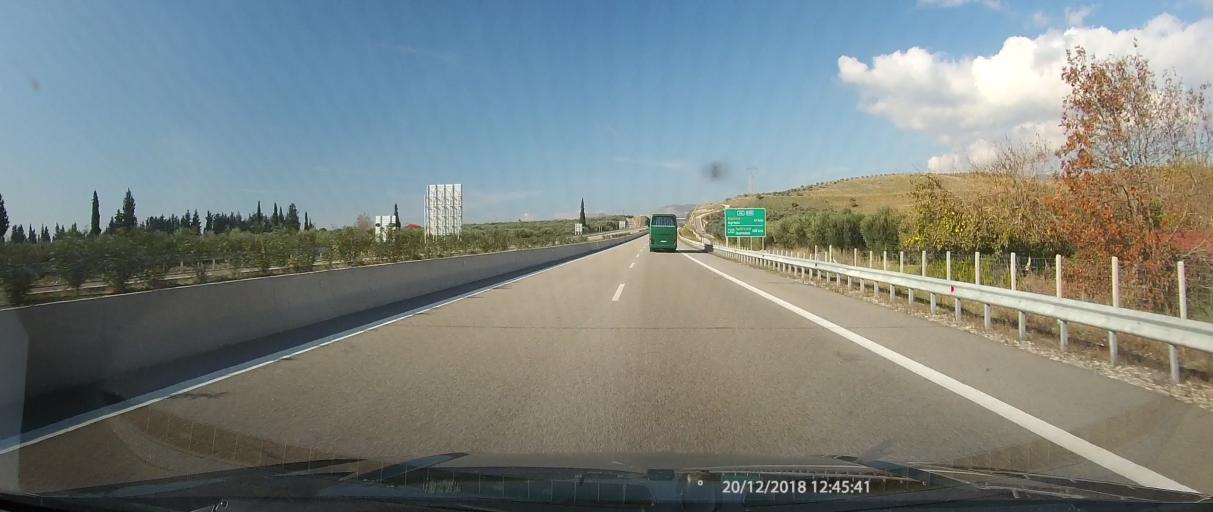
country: GR
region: West Greece
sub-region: Nomos Aitolias kai Akarnanias
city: Mesolongi
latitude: 38.3833
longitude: 21.4900
